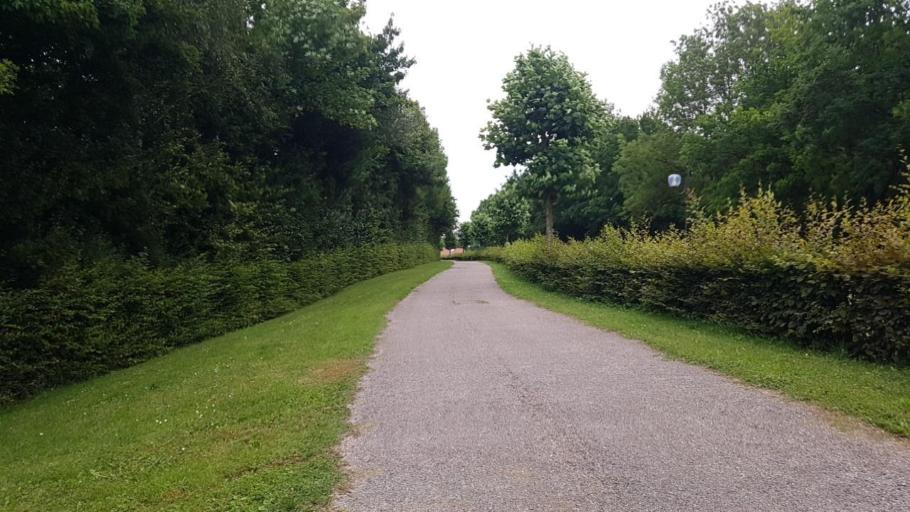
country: FR
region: Picardie
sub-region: Departement de l'Aisne
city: Hirson
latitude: 49.9122
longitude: 4.0603
